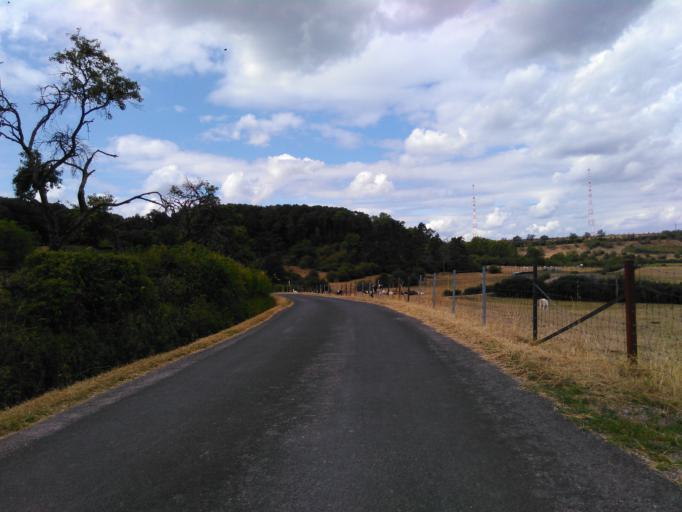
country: LU
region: Grevenmacher
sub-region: Canton de Grevenmacher
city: Junglinster
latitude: 49.7055
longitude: 6.2726
